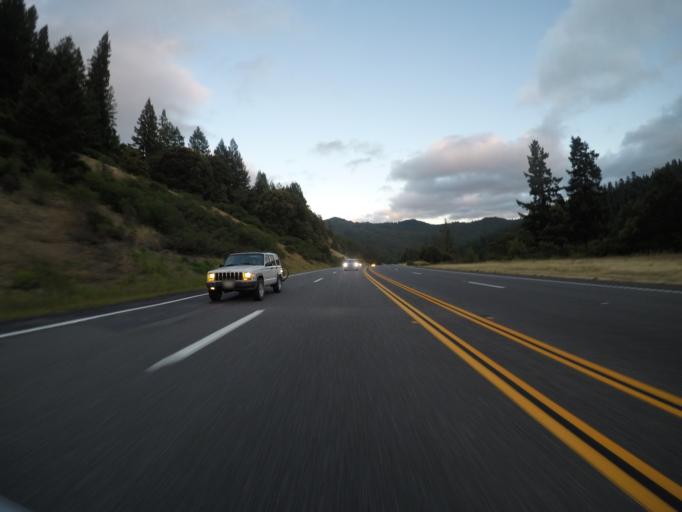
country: US
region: California
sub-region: Humboldt County
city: Redway
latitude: 40.0458
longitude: -123.7831
